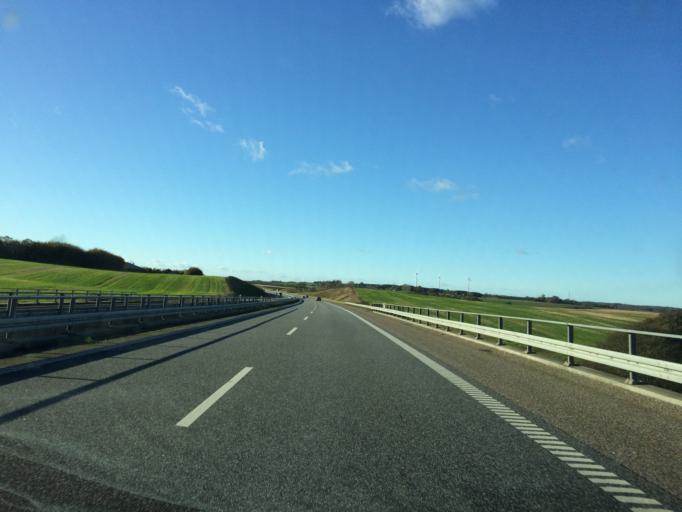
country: DK
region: Central Jutland
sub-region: Hedensted Kommune
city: Torring
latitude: 55.8317
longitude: 9.5126
